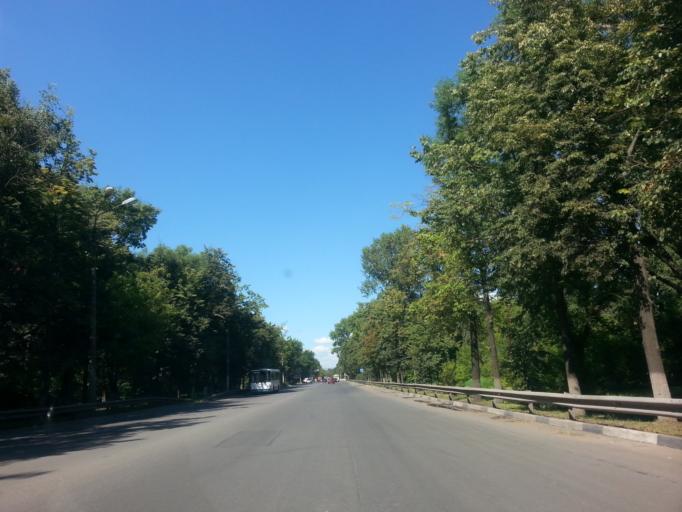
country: RU
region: Nizjnij Novgorod
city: Gorbatovka
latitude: 56.3421
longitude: 43.8425
